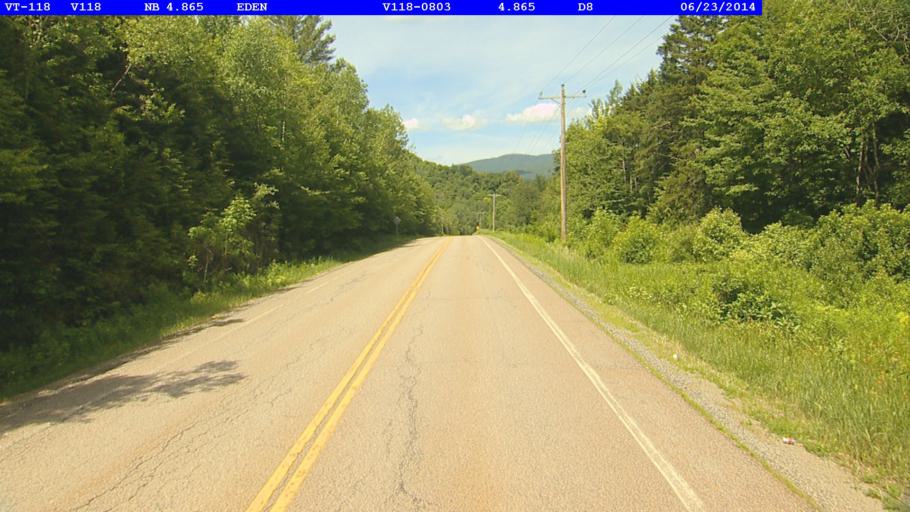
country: US
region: Vermont
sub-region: Lamoille County
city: Johnson
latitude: 44.7629
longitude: -72.5917
